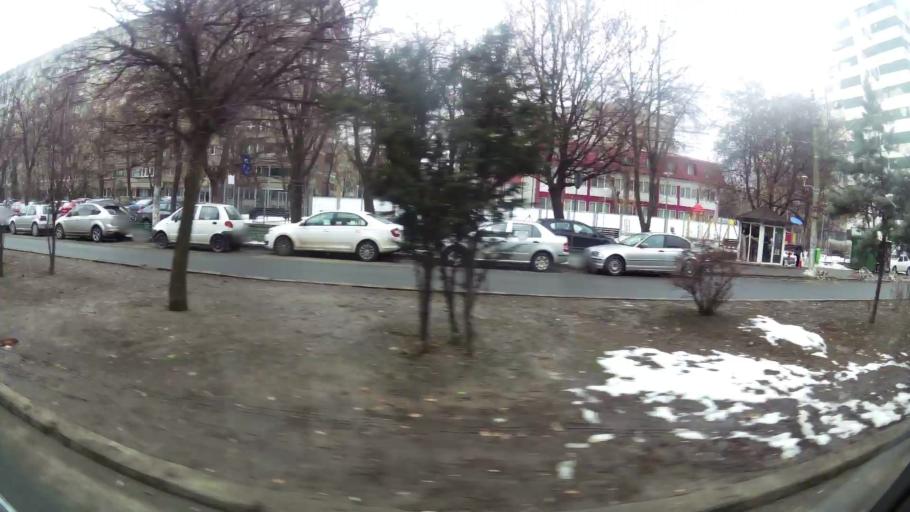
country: RO
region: Ilfov
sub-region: Comuna Chiajna
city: Rosu
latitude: 44.4231
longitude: 26.0472
